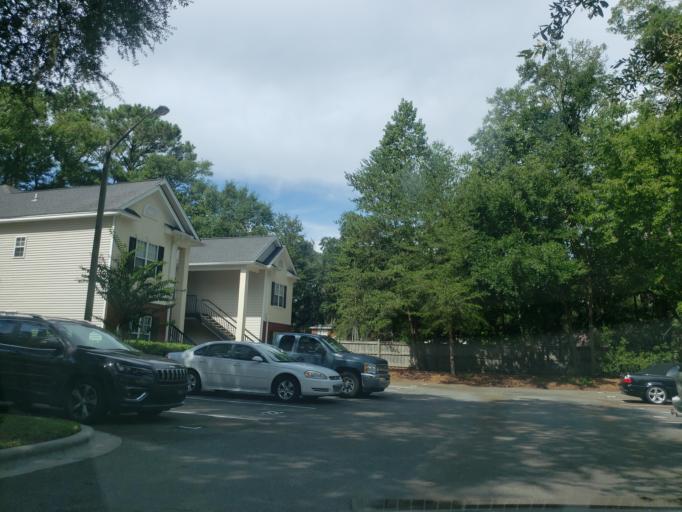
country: US
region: Georgia
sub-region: Chatham County
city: Wilmington Island
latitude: 32.0276
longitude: -80.9647
